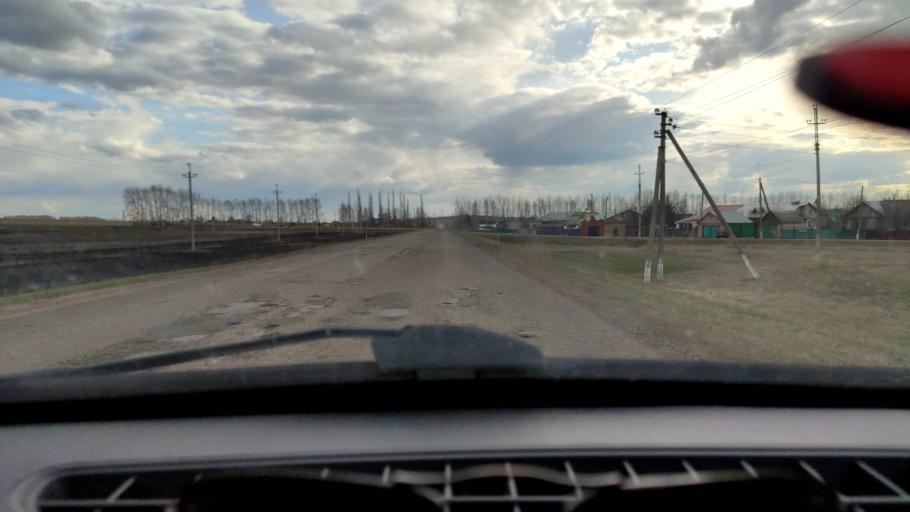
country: RU
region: Bashkortostan
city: Karmaskaly
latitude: 54.3924
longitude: 56.2407
